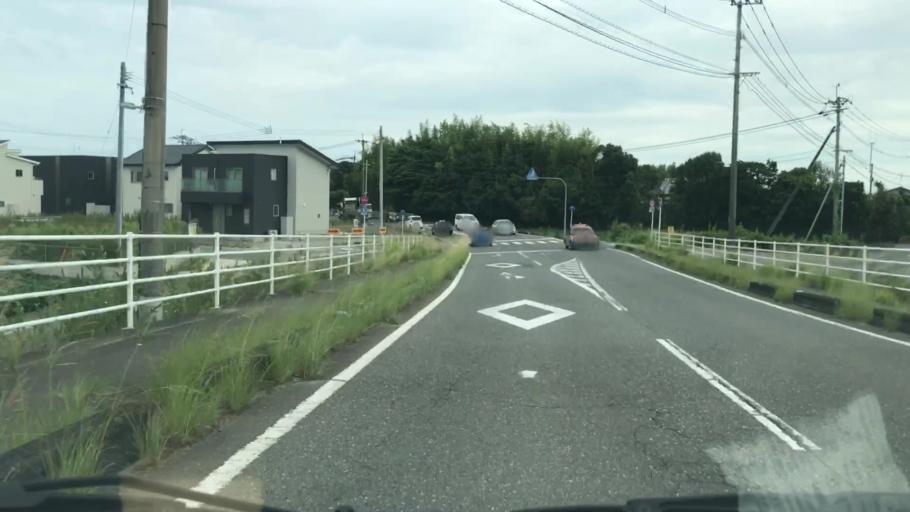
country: JP
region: Saga Prefecture
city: Saga-shi
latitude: 33.2765
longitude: 130.2556
